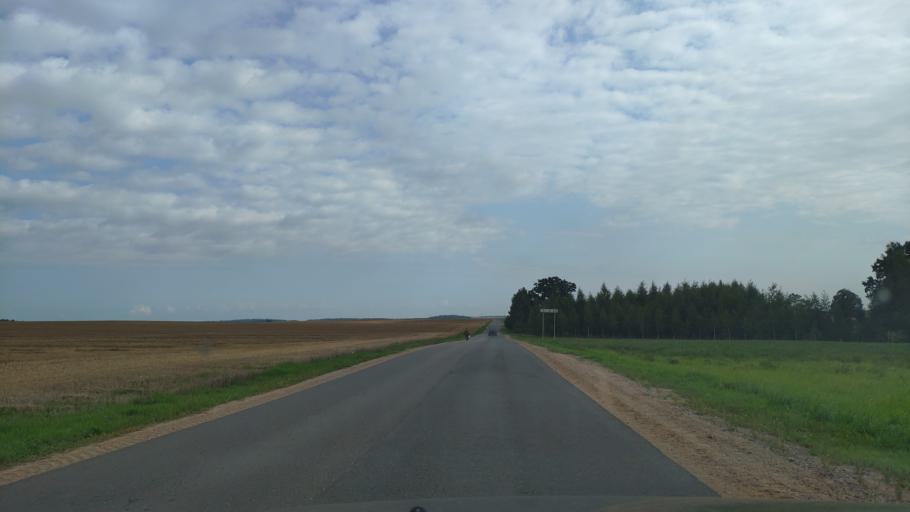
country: BY
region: Minsk
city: Khatsyezhyna
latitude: 53.8351
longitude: 27.3066
